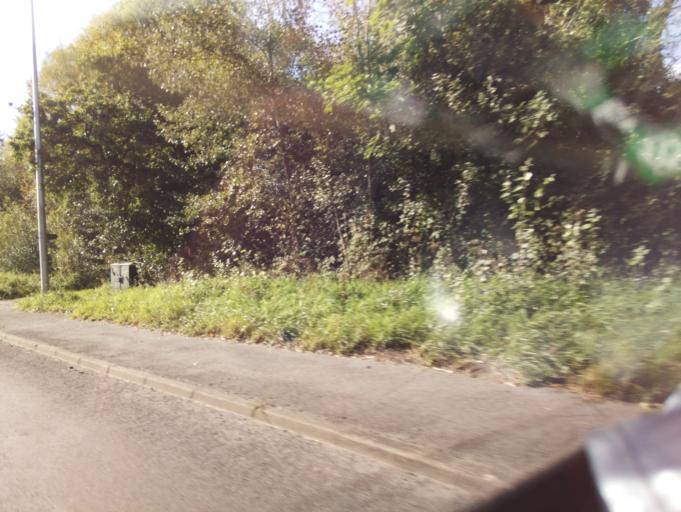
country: GB
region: England
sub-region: Hampshire
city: Tadley
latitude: 51.4016
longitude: -1.1420
